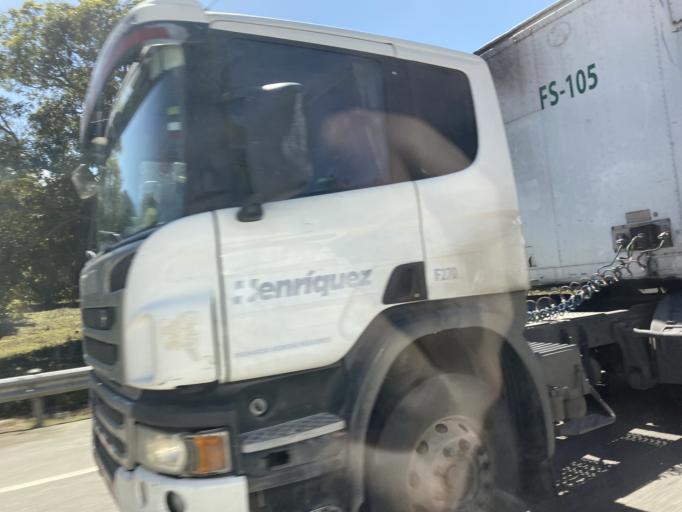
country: DO
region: Puerto Plata
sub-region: Puerto Plata
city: Puerto Plata
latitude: 19.8302
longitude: -70.7647
